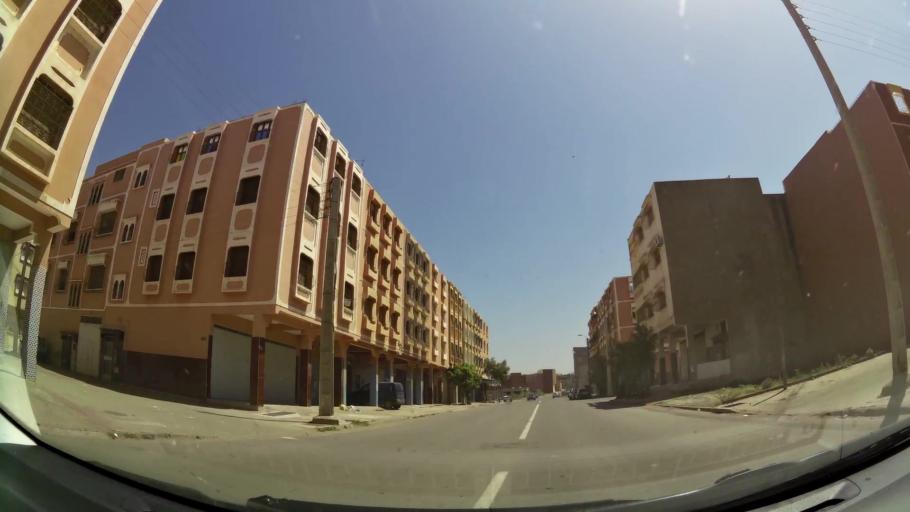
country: MA
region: Souss-Massa-Draa
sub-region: Inezgane-Ait Mellou
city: Inezgane
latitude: 30.3359
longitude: -9.4994
